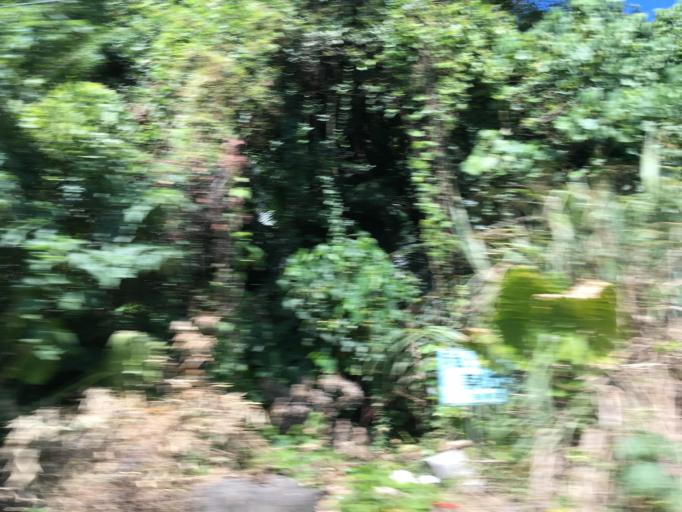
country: TW
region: Taipei
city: Taipei
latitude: 25.1516
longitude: 121.5038
